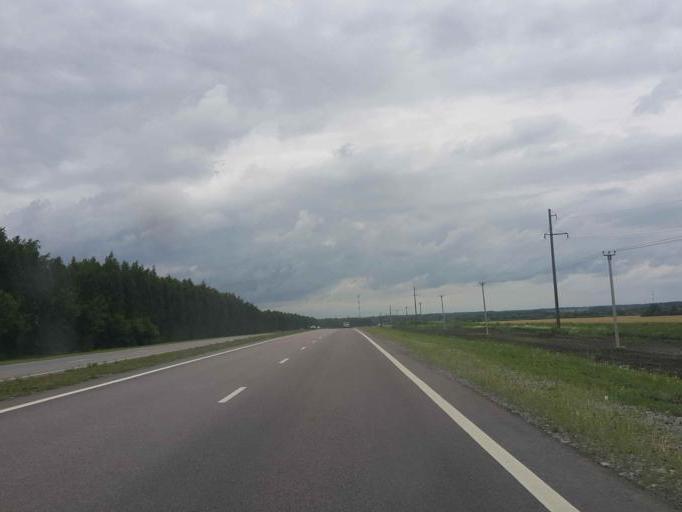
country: RU
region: Tambov
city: Zavoronezhskoye
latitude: 52.8813
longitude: 40.7333
